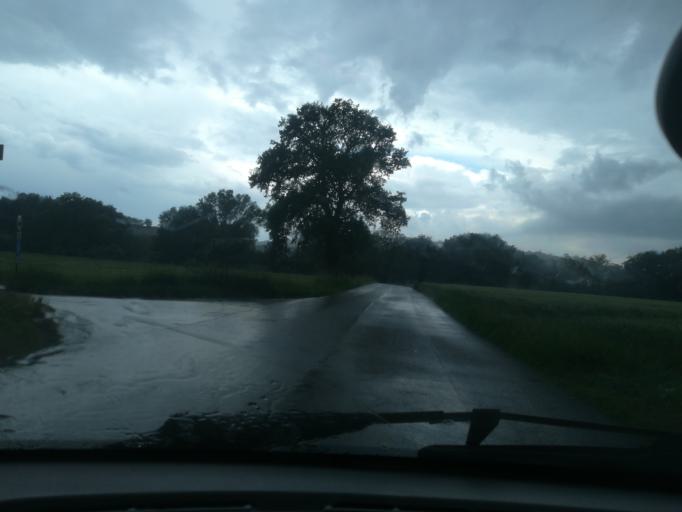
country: IT
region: The Marches
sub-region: Provincia di Macerata
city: Passo di Treia
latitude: 43.3106
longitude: 13.3440
